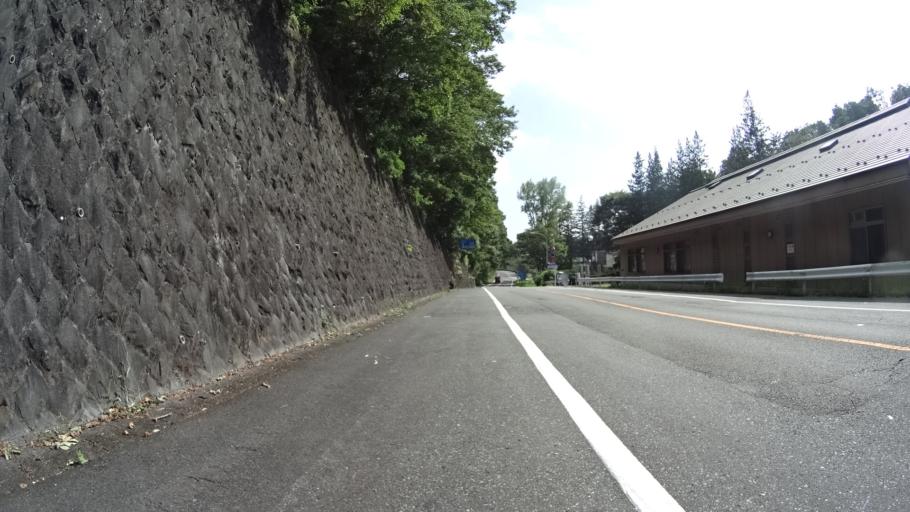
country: JP
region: Yamanashi
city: Kofu-shi
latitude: 35.7148
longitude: 138.5535
